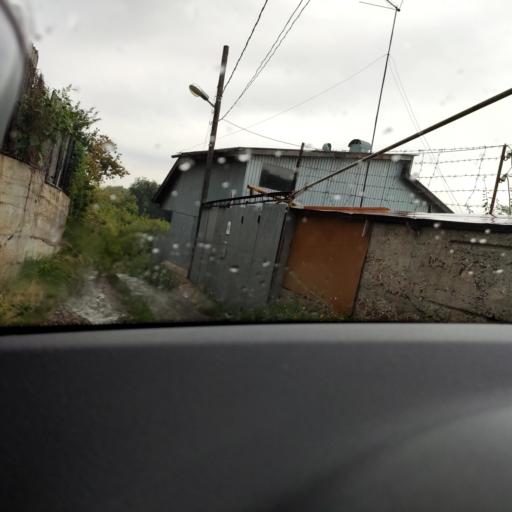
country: RU
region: Samara
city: Samara
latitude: 53.1730
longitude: 50.1573
